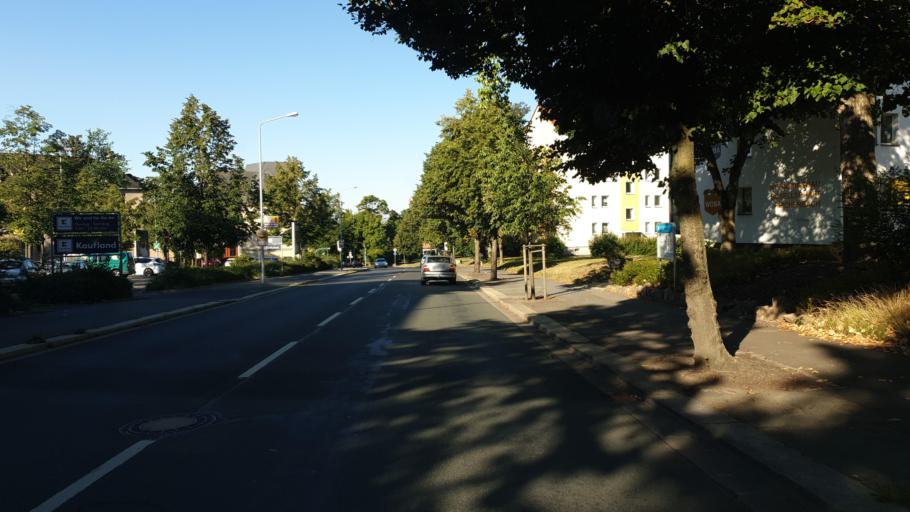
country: DE
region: Saxony
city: Reichenbach/Vogtland
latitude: 50.6312
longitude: 12.3102
